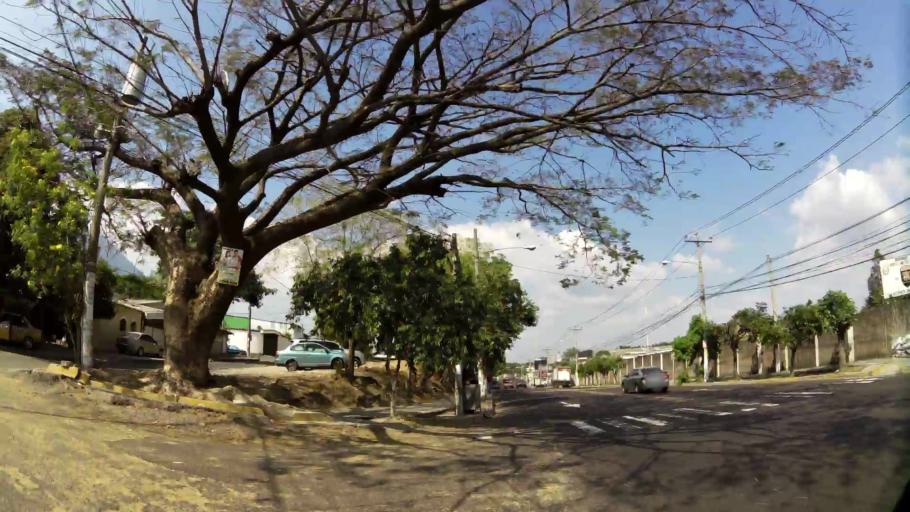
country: SV
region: San Salvador
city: Mejicanos
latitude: 13.7190
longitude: -89.2167
